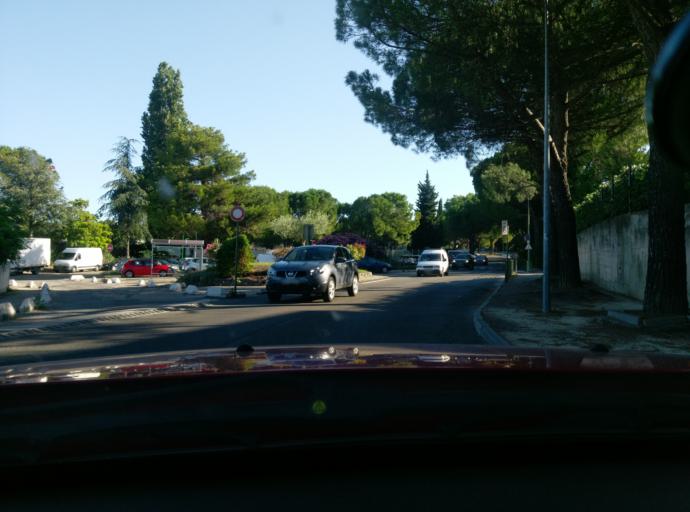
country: FR
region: Languedoc-Roussillon
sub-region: Departement du Gard
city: Uzes
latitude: 44.0095
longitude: 4.4146
